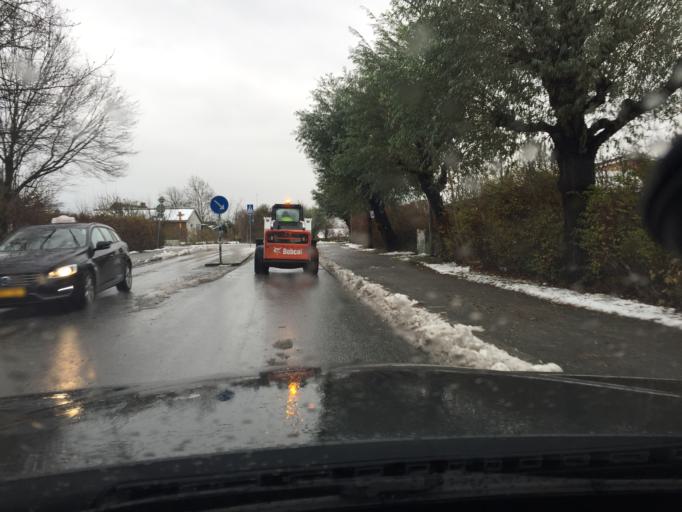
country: SE
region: Skane
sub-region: Lunds Kommun
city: Lund
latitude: 55.7064
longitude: 13.2311
